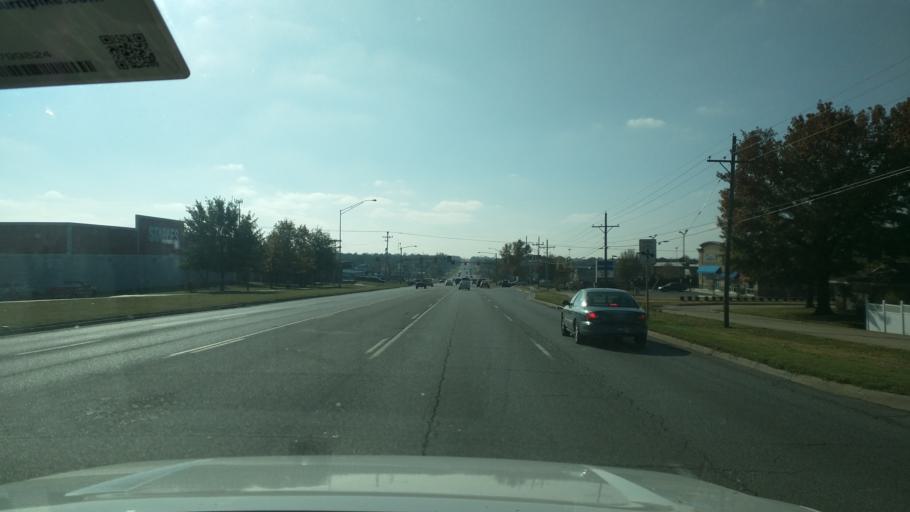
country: US
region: Oklahoma
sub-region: Washington County
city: Bartlesville
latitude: 36.7154
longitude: -95.9352
